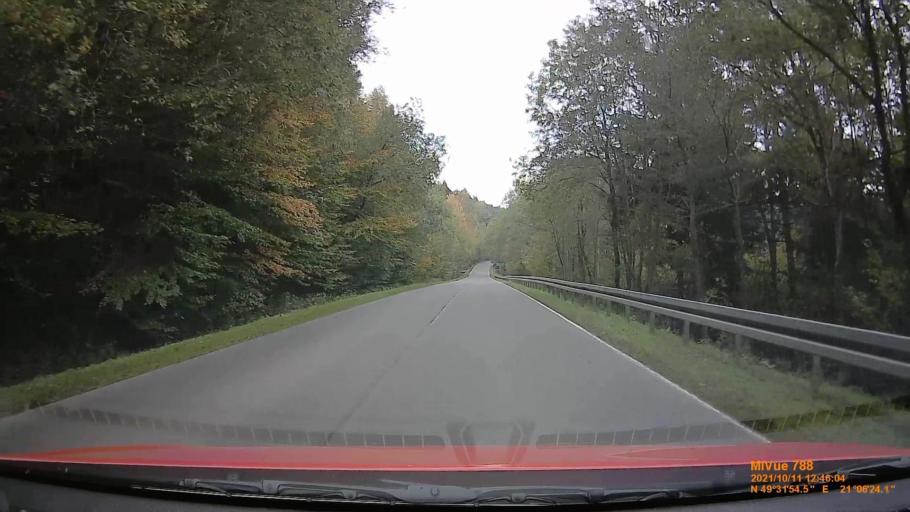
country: PL
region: Lesser Poland Voivodeship
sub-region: Powiat gorlicki
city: Uscie Gorlickie
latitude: 49.5319
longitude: 21.1064
